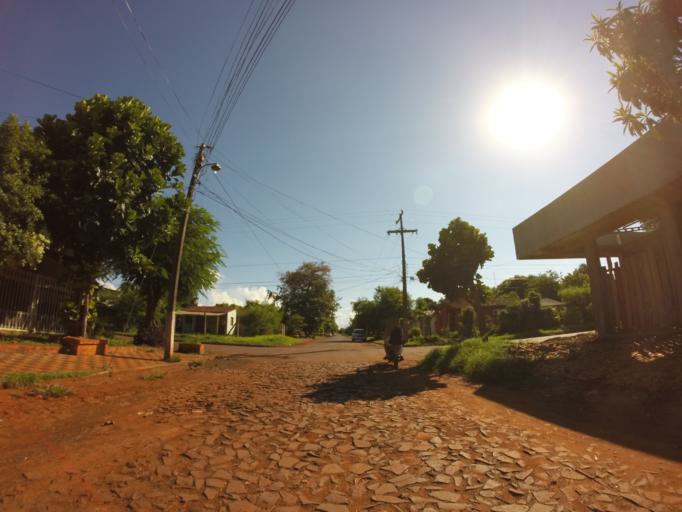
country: PY
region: Alto Parana
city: Ciudad del Este
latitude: -25.3757
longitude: -54.6496
